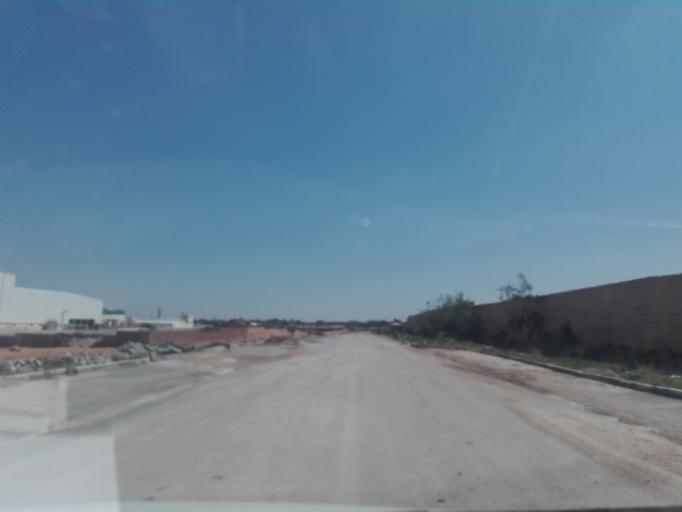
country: TN
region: Safaqis
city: Sfax
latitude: 34.7258
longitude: 10.5192
